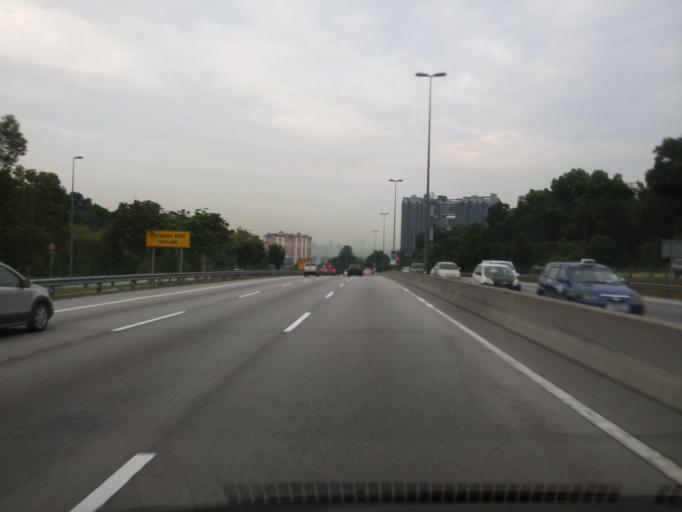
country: MY
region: Kuala Lumpur
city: Kuala Lumpur
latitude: 3.0798
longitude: 101.6915
